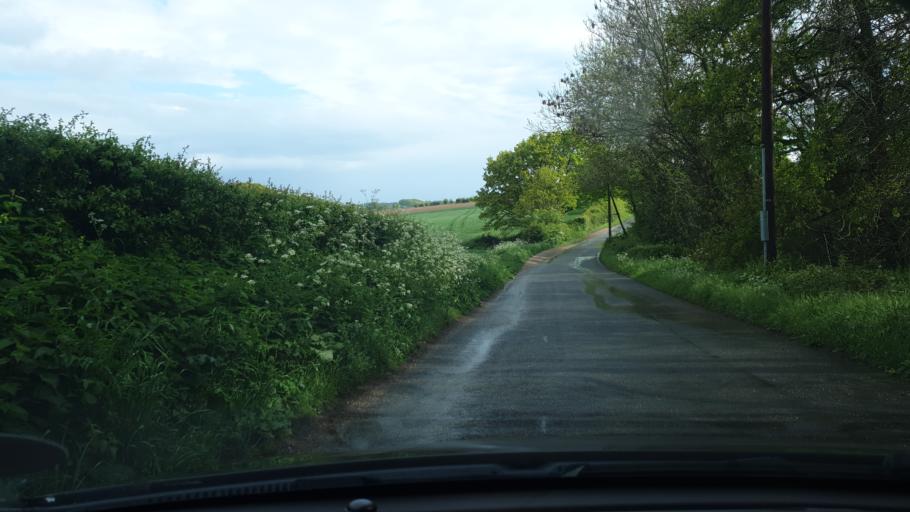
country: GB
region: England
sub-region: Essex
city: Great Bentley
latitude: 51.8428
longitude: 1.0507
